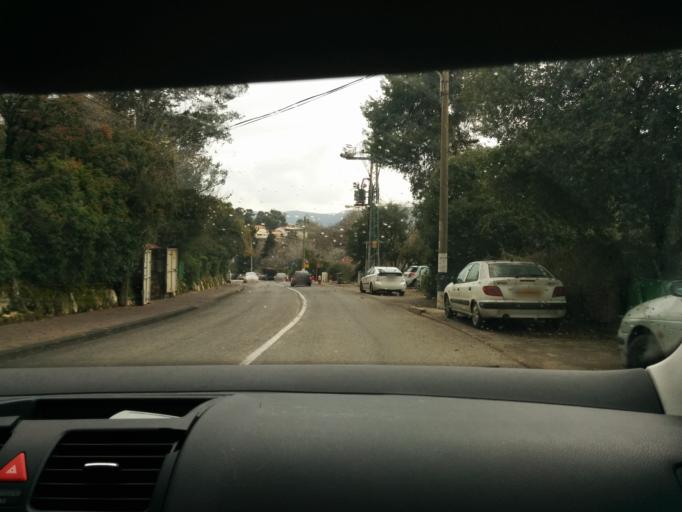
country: IL
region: Northern District
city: Basmat Tab`un
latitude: 32.7253
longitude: 35.1348
